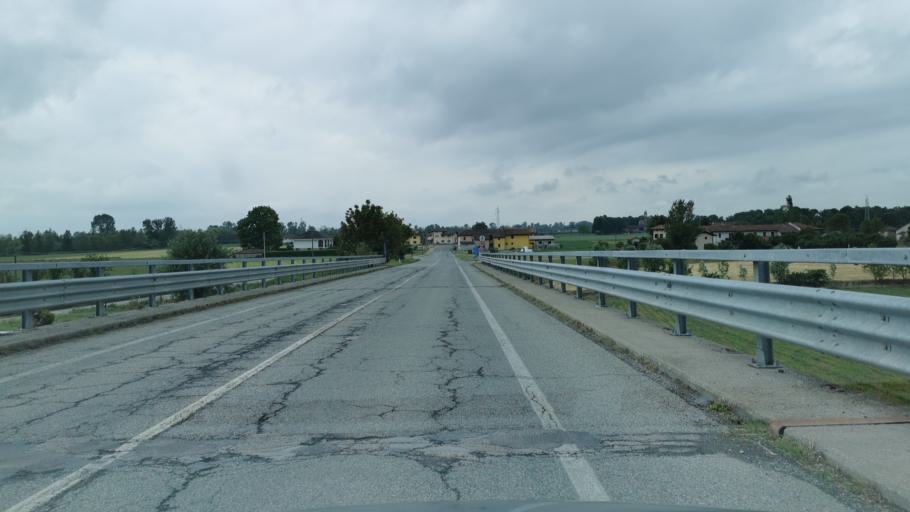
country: IT
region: Piedmont
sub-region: Provincia di Cuneo
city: Savigliano
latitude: 44.6362
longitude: 7.6424
